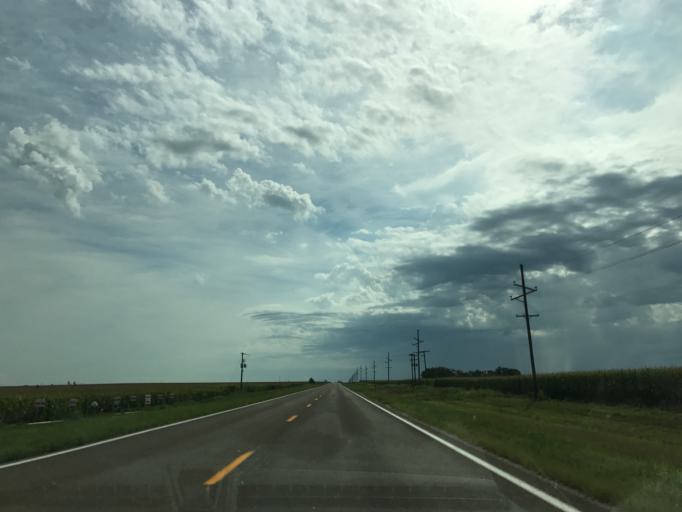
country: US
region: Nebraska
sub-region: Jefferson County
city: Fairbury
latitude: 40.3061
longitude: -97.1118
